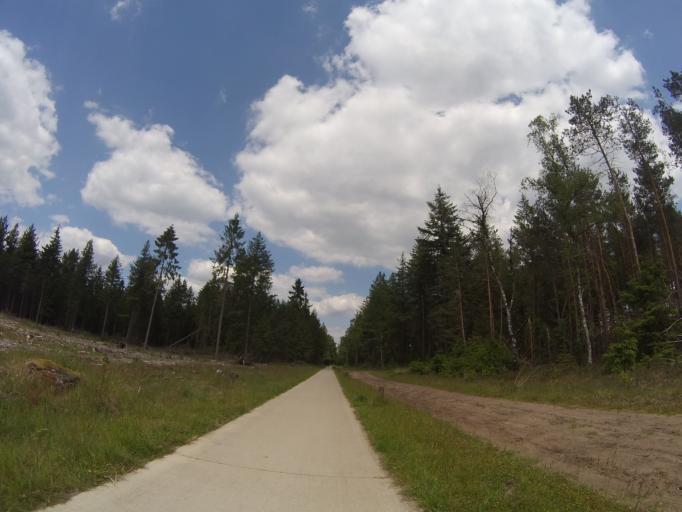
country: NL
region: Gelderland
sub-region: Gemeente Ede
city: Harskamp
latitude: 52.1749
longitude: 5.7616
